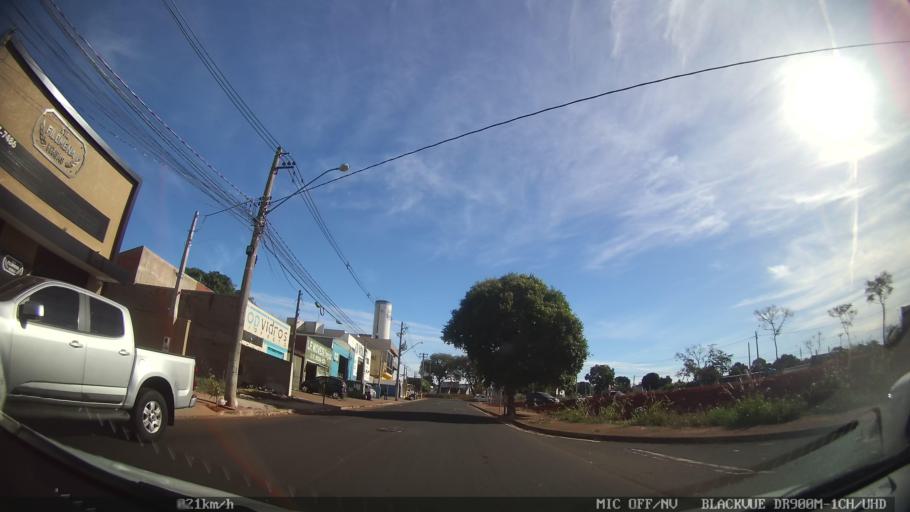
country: BR
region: Sao Paulo
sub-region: Sao Jose Do Rio Preto
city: Sao Jose do Rio Preto
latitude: -20.7850
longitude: -49.3525
